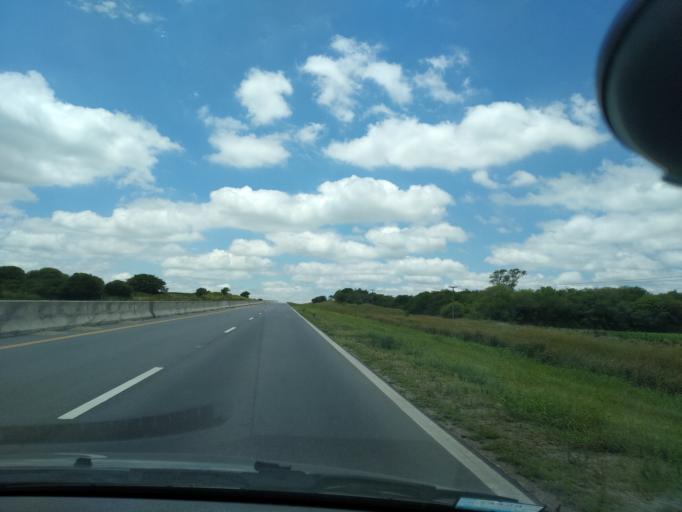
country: AR
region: Cordoba
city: Alta Gracia
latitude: -31.6524
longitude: -64.3332
